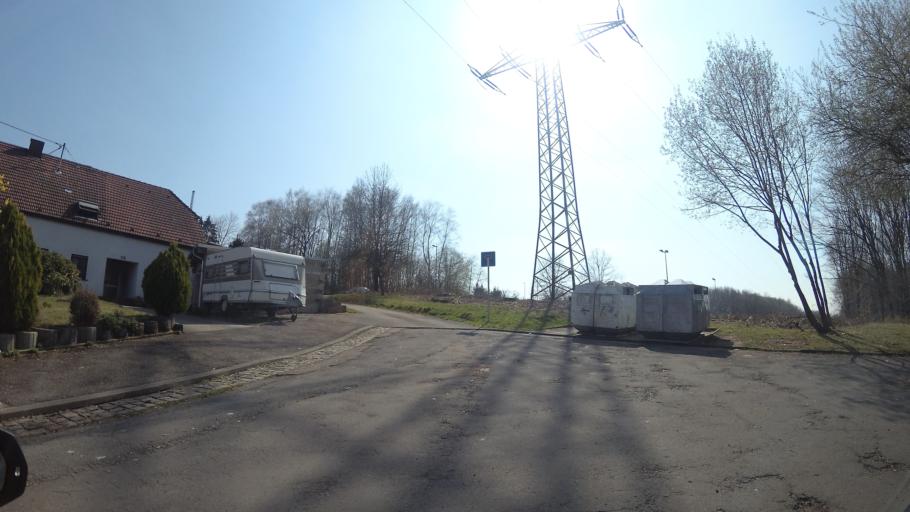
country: DE
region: Saarland
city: Quierschied
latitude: 49.3114
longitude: 7.0570
